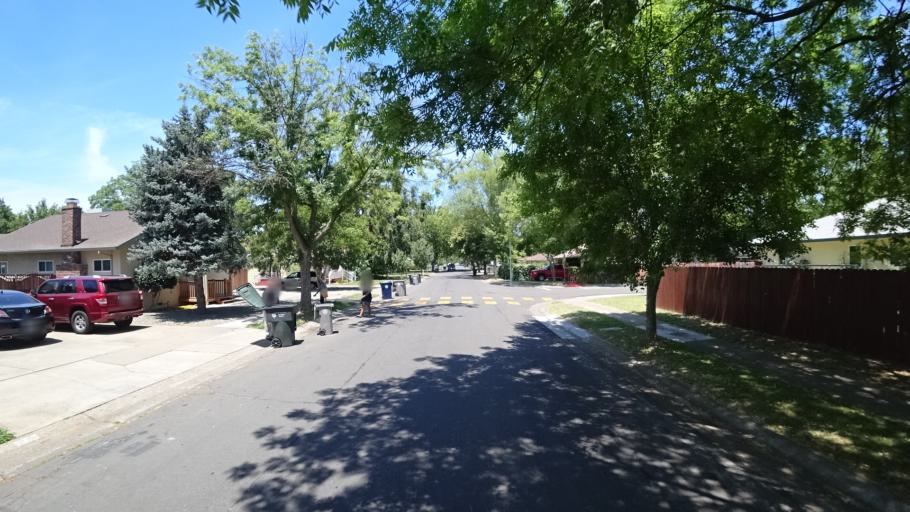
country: US
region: California
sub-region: Sacramento County
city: Florin
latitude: 38.5330
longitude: -121.4211
